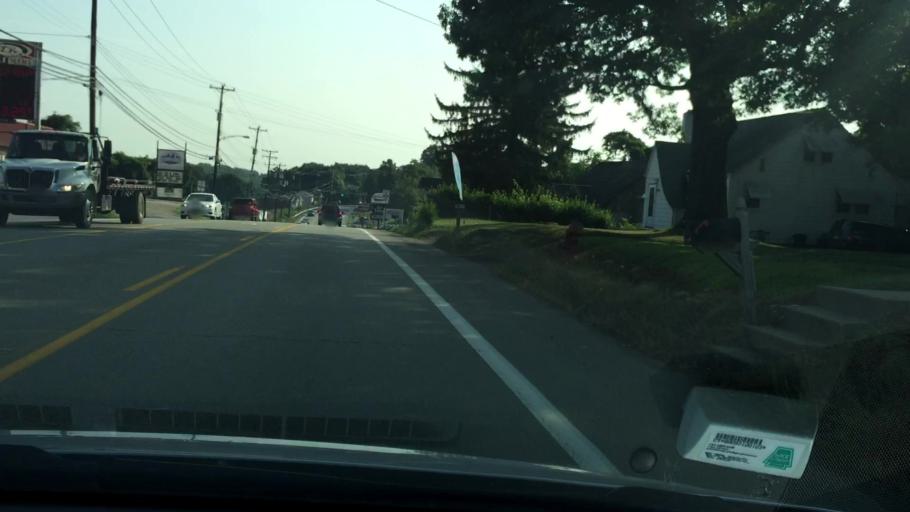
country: US
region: Pennsylvania
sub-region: Allegheny County
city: Rennerdale
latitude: 40.4482
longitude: -80.1425
